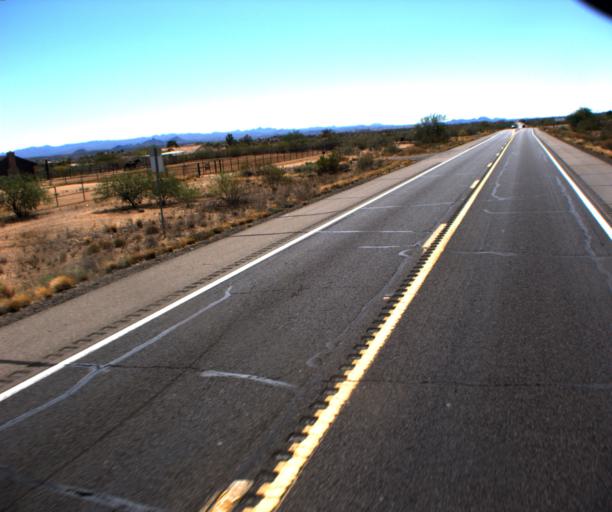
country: US
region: Arizona
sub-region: Maricopa County
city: Wickenburg
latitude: 34.0398
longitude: -112.8305
